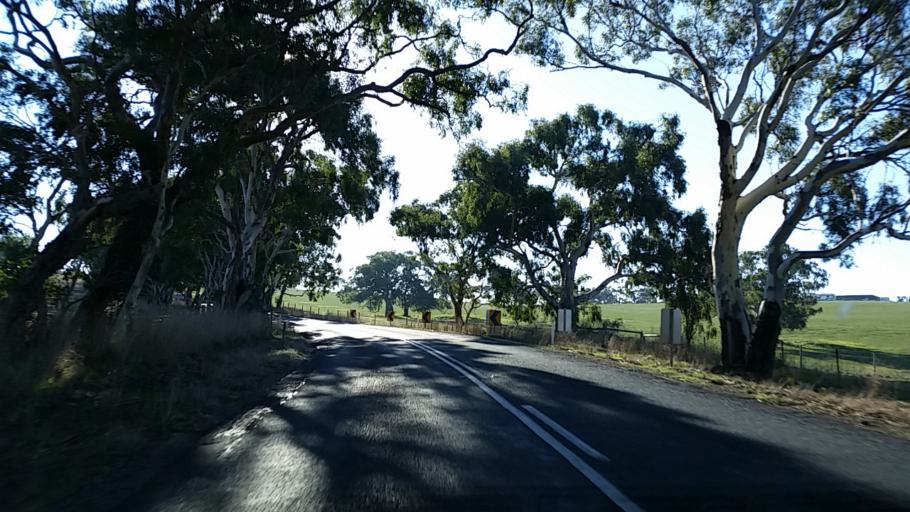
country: AU
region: South Australia
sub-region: Mount Barker
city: Mount Barker
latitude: -35.1298
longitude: 138.9111
